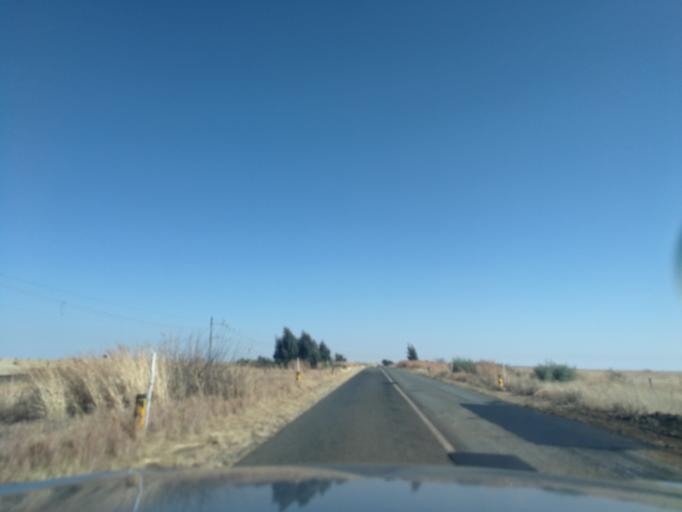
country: ZA
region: Orange Free State
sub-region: Fezile Dabi District Municipality
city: Kroonstad
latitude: -27.8933
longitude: 27.4895
